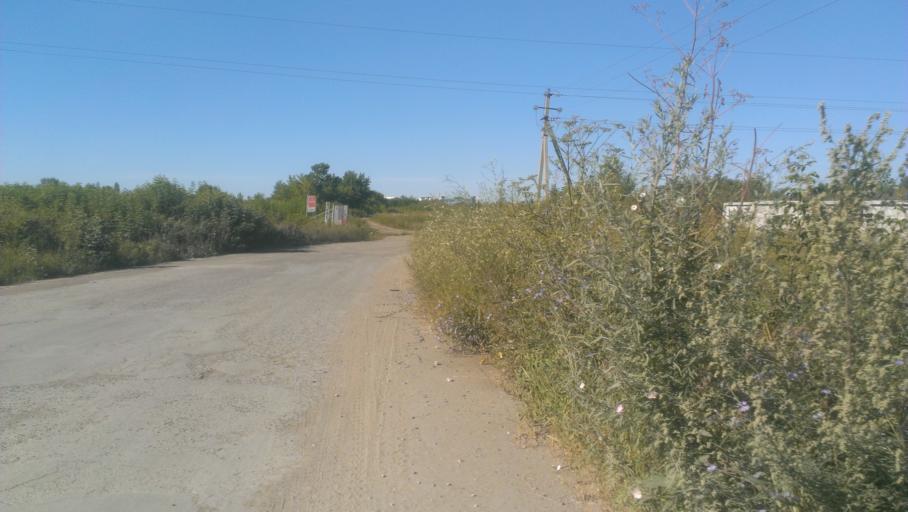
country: RU
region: Altai Krai
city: Novosilikatnyy
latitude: 53.3358
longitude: 83.6352
